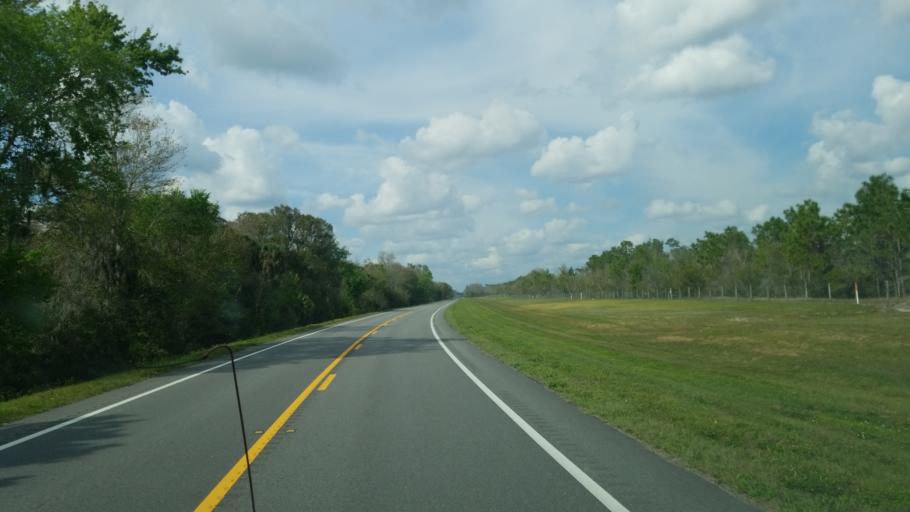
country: US
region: Florida
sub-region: Indian River County
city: Fellsmere
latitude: 27.7670
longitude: -80.9167
